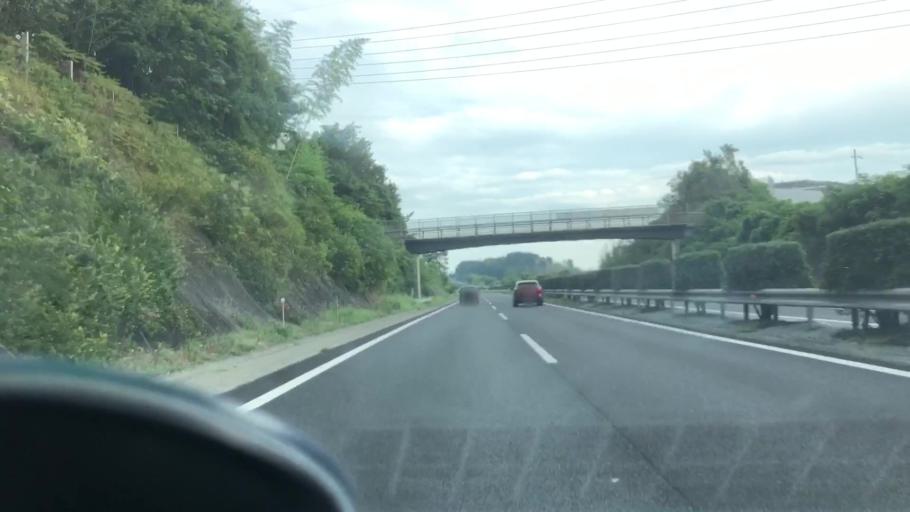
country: JP
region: Hyogo
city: Yashiro
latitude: 34.9374
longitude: 134.8820
